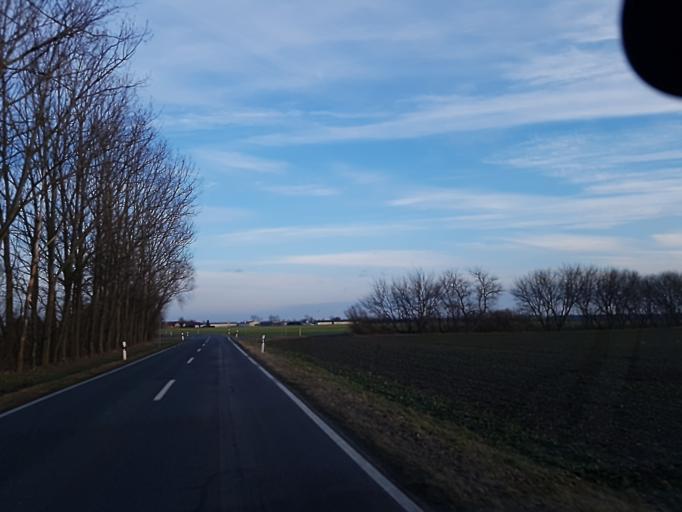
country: DE
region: Brandenburg
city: Juterbog
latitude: 51.9218
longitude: 13.0710
